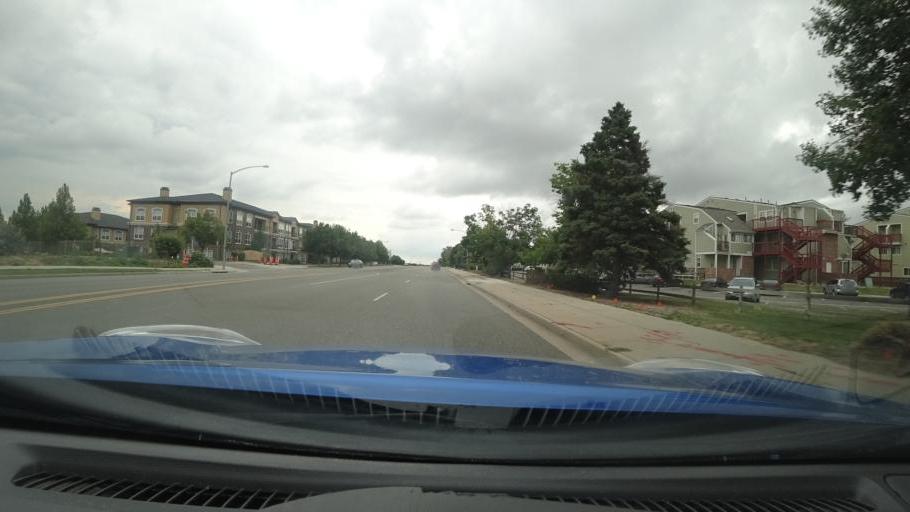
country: US
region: Colorado
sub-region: Adams County
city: Aurora
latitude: 39.6991
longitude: -104.8191
